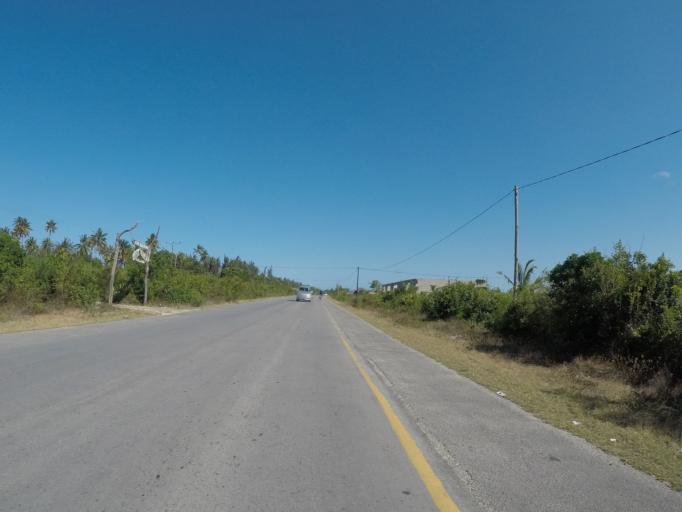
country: TZ
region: Zanzibar Central/South
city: Nganane
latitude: -6.2745
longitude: 39.5333
